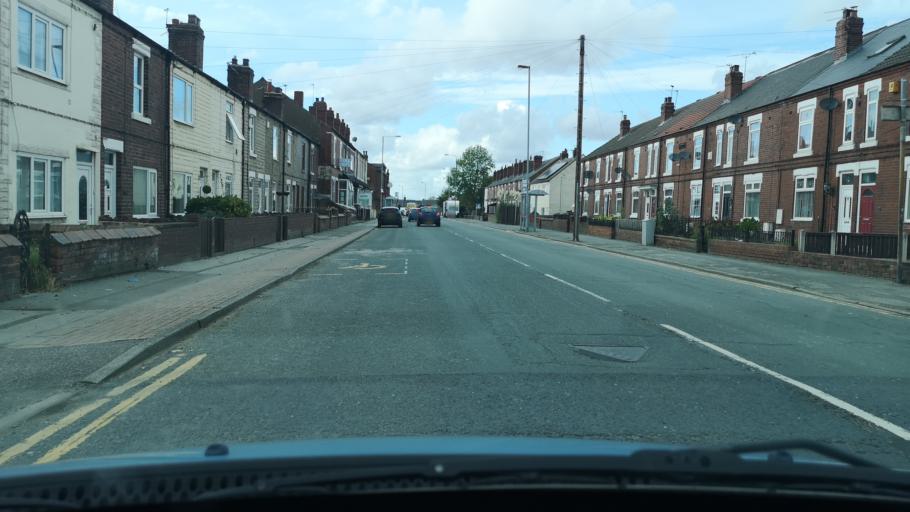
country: GB
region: England
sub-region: City and Borough of Wakefield
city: Featherstone
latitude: 53.6740
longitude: -1.3510
